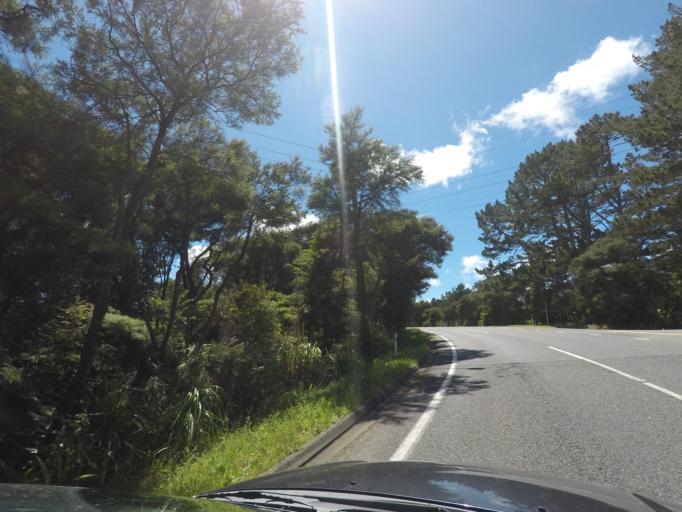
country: NZ
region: Auckland
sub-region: Auckland
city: Rothesay Bay
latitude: -36.7608
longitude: 174.6585
